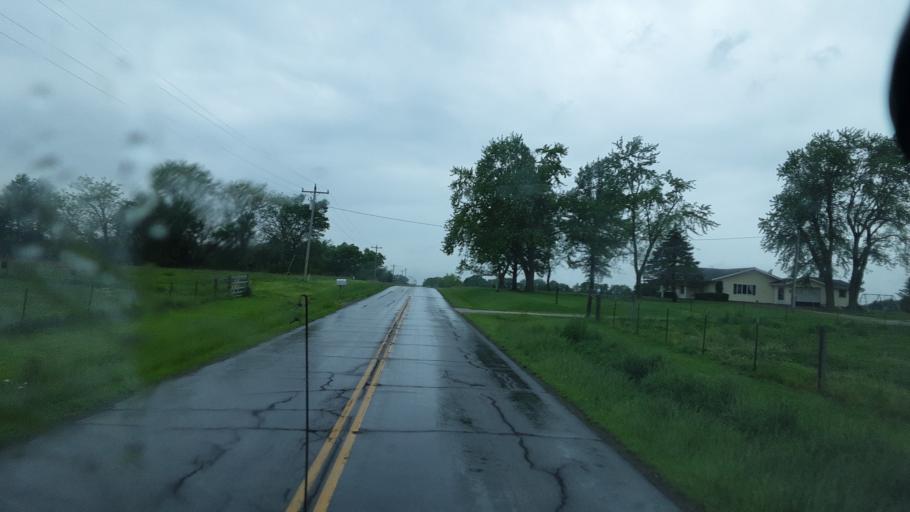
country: US
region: Missouri
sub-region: Randolph County
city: Moberly
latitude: 39.3928
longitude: -92.2373
